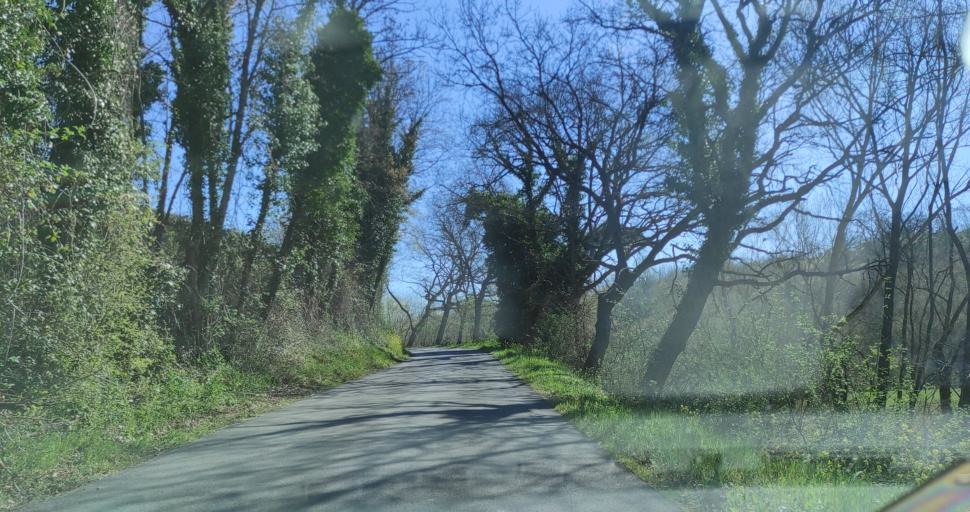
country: IT
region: The Marches
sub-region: Provincia di Macerata
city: Piediripa
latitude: 43.3126
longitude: 13.4861
